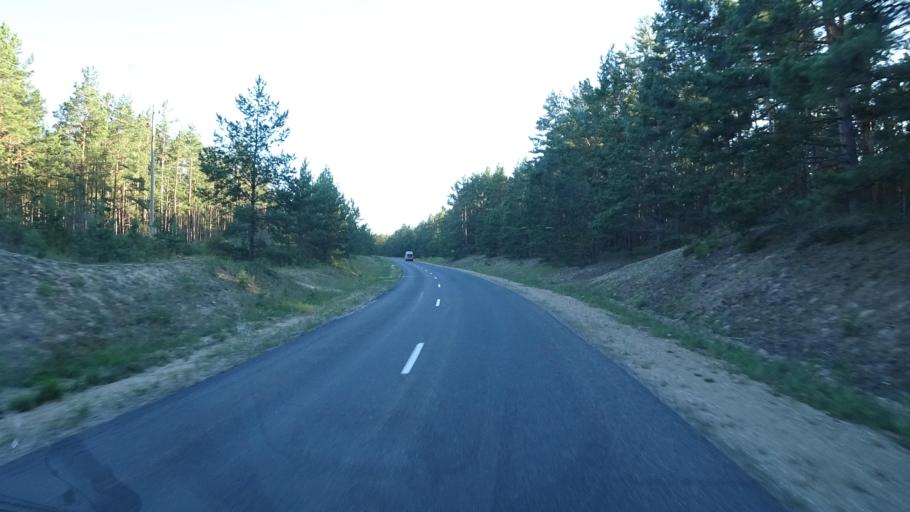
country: LV
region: Dundaga
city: Dundaga
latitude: 57.7203
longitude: 22.5746
